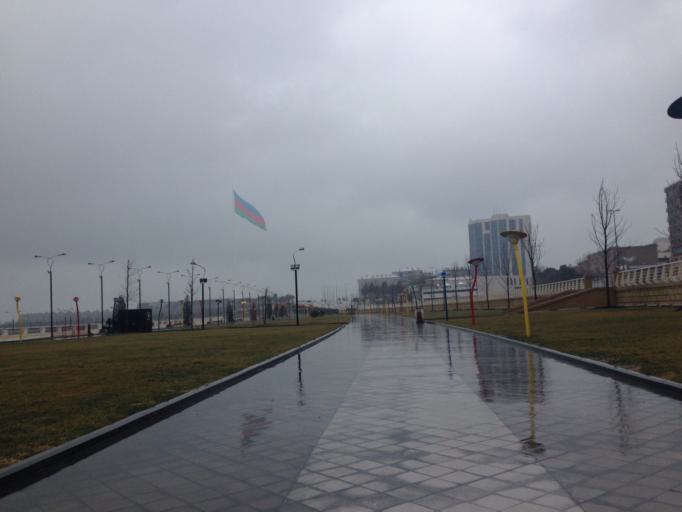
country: AZ
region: Baki
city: Badamdar
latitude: 40.3496
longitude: 49.8369
